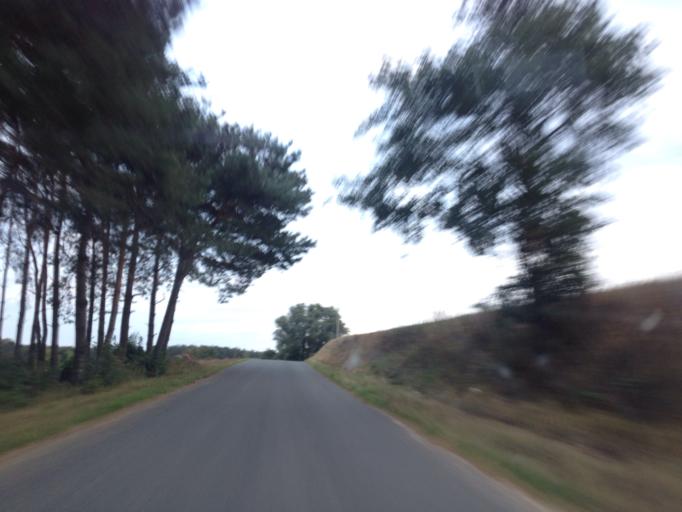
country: PL
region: Kujawsko-Pomorskie
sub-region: Powiat brodnicki
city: Brzozie
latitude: 53.2930
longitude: 19.6909
